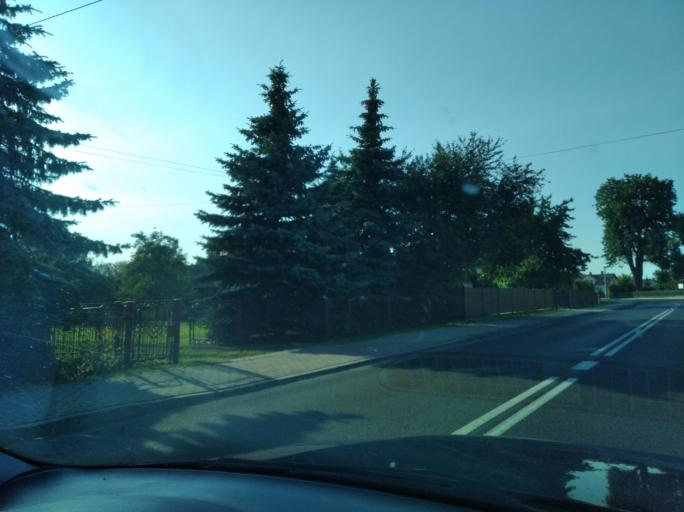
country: PL
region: Subcarpathian Voivodeship
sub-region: Powiat lezajski
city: Stare Miasto
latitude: 50.2847
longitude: 22.4298
